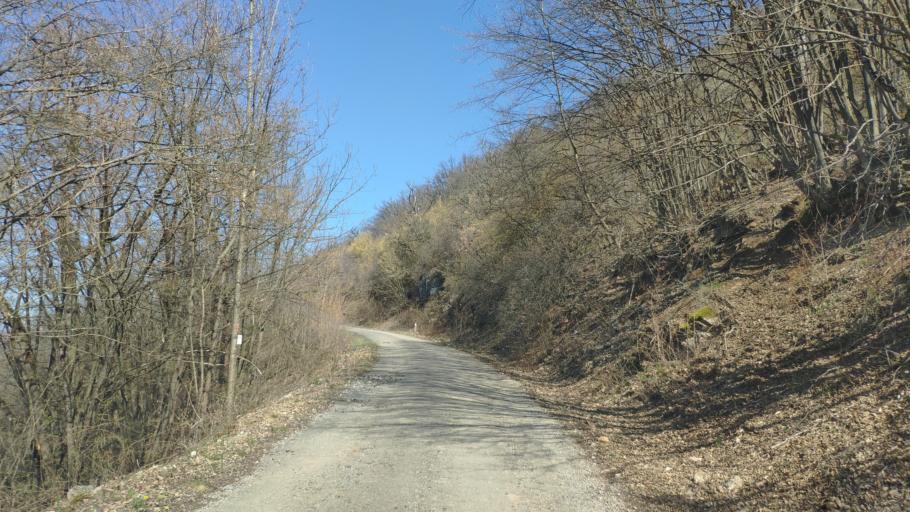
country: SK
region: Kosicky
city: Roznava
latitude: 48.5762
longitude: 20.4058
